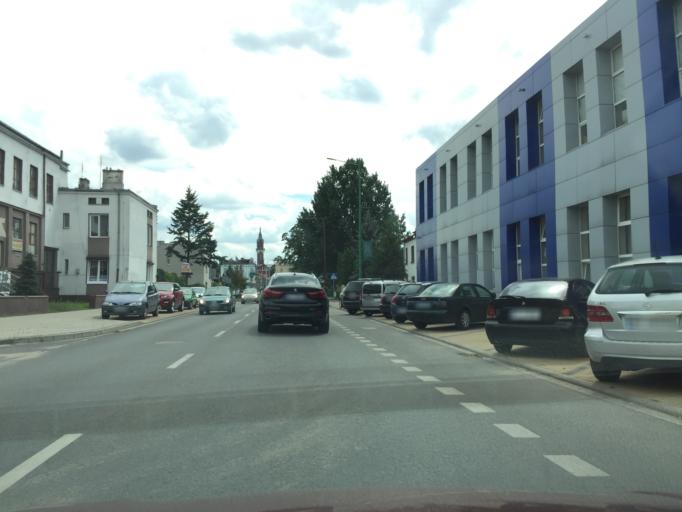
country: PL
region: Greater Poland Voivodeship
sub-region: Kalisz
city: Kalisz
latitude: 51.7536
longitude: 18.0943
